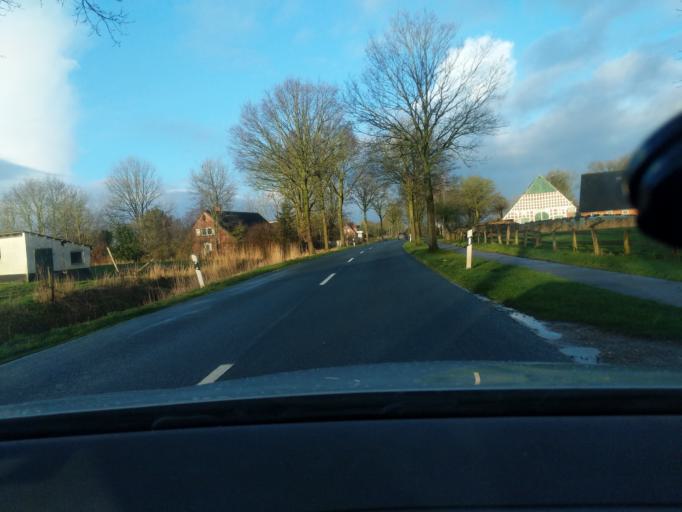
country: DE
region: Lower Saxony
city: Cuxhaven
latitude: 53.8336
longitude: 8.7038
